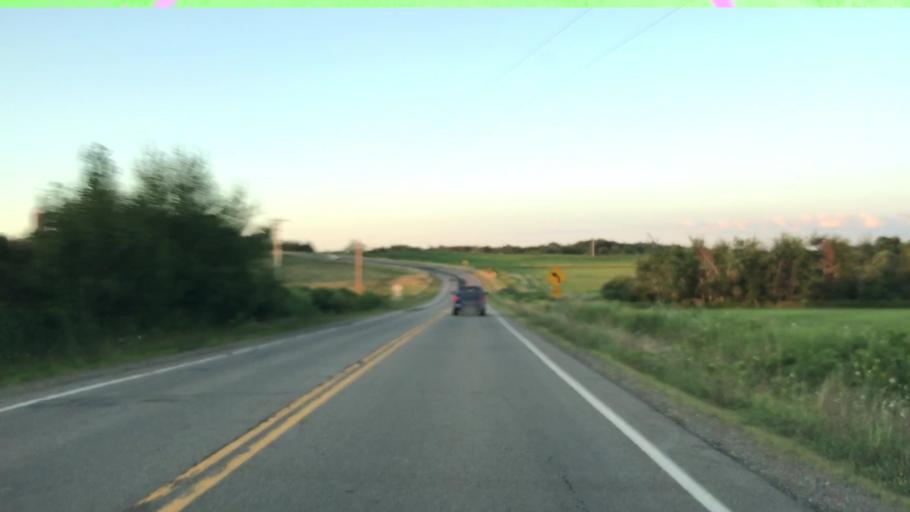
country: US
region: New York
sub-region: Chautauqua County
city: Fredonia
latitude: 42.3592
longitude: -79.3578
